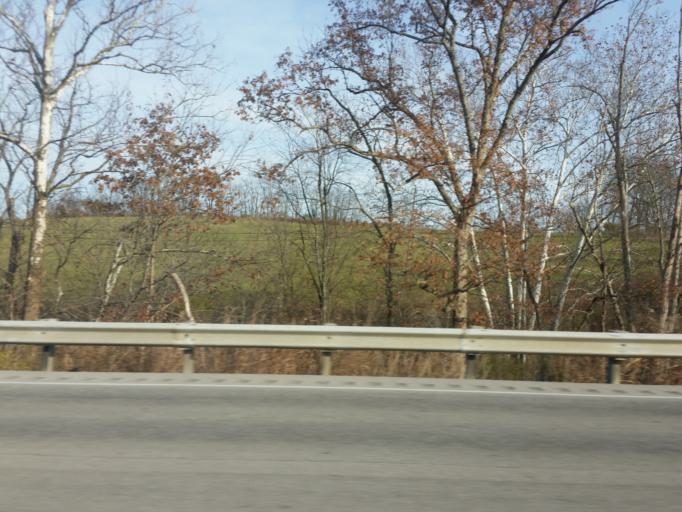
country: US
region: Kentucky
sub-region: Harrison County
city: Cynthiana
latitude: 38.4379
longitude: -84.2850
